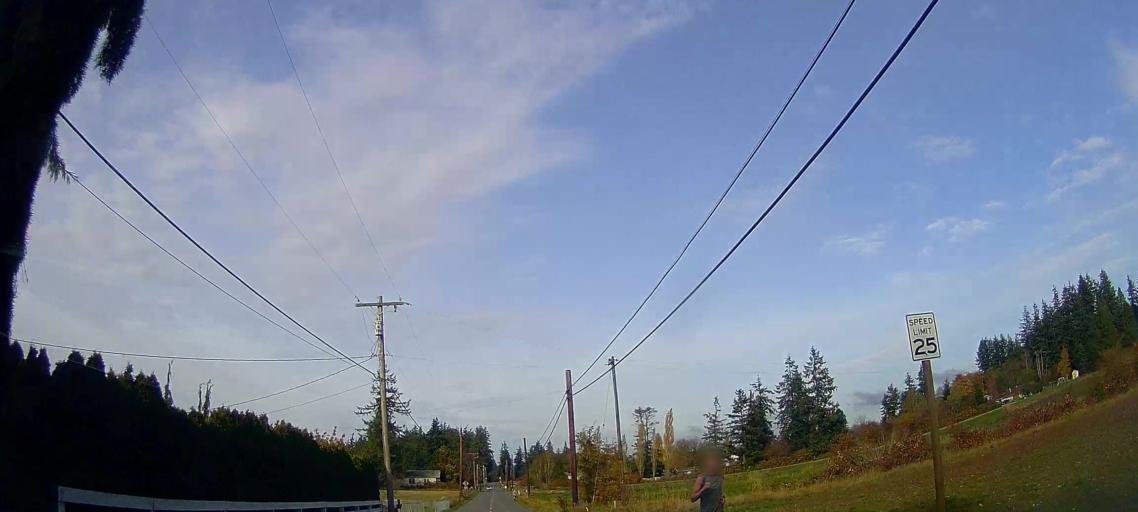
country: US
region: Washington
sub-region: Snohomish County
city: Stanwood
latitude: 48.2507
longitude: -122.3411
